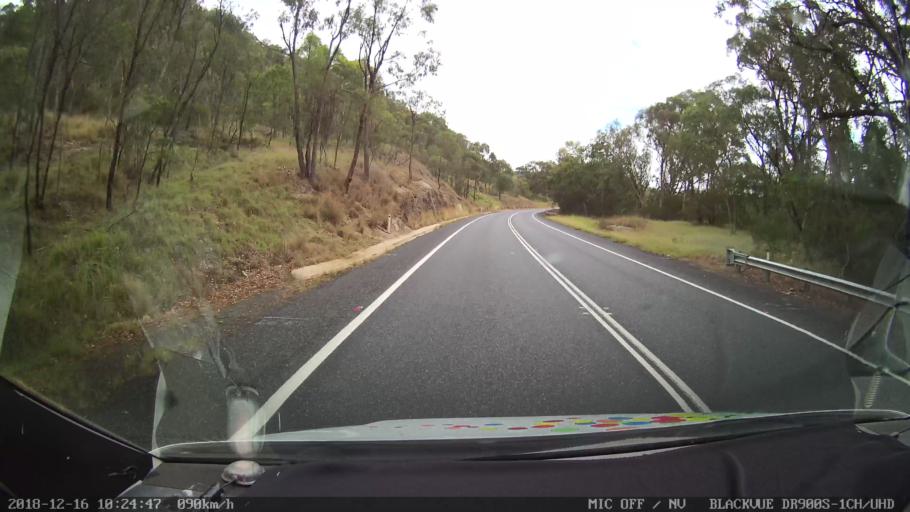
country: AU
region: New South Wales
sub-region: Tenterfield Municipality
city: Carrolls Creek
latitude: -29.1669
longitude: 152.0032
